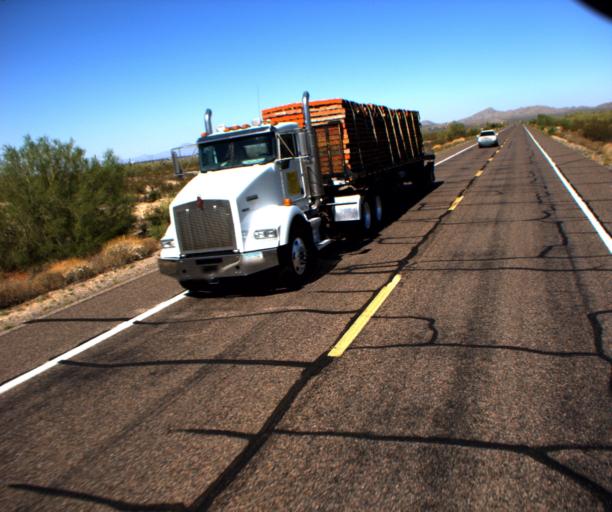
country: US
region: Arizona
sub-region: Pinal County
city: Sacaton
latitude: 33.0037
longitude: -111.7318
